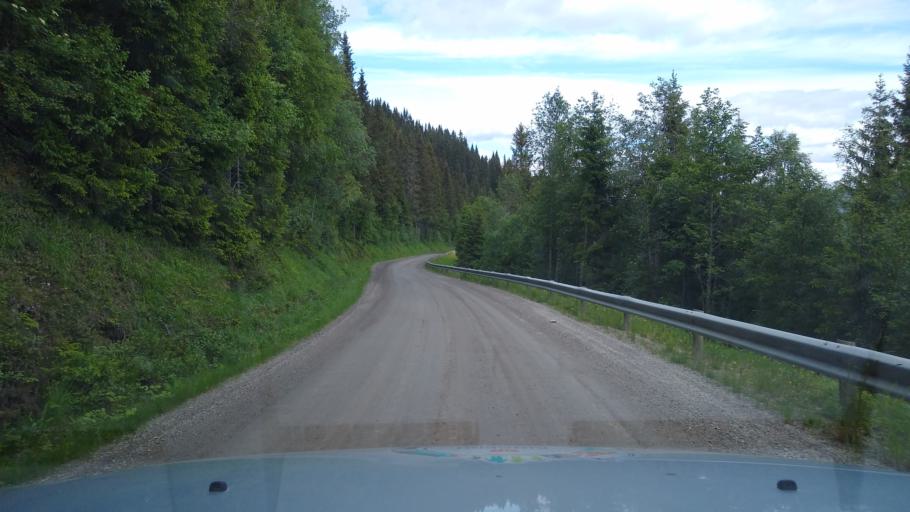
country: NO
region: Oppland
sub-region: Ringebu
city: Ringebu
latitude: 61.4980
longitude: 10.1433
